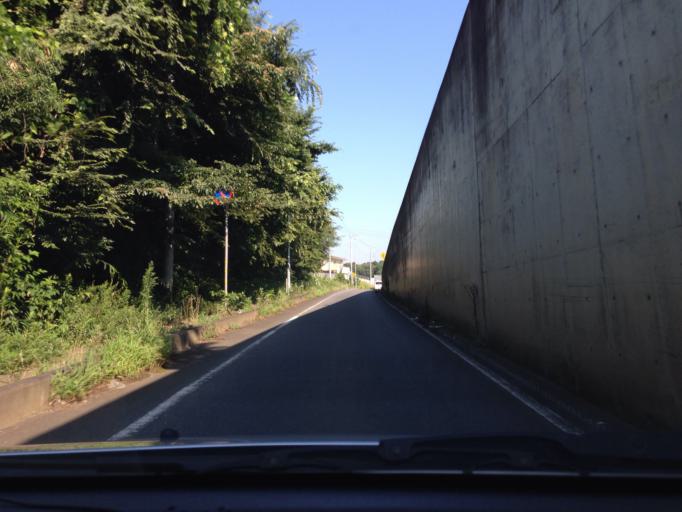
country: JP
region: Ibaraki
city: Naka
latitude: 36.0498
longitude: 140.1854
